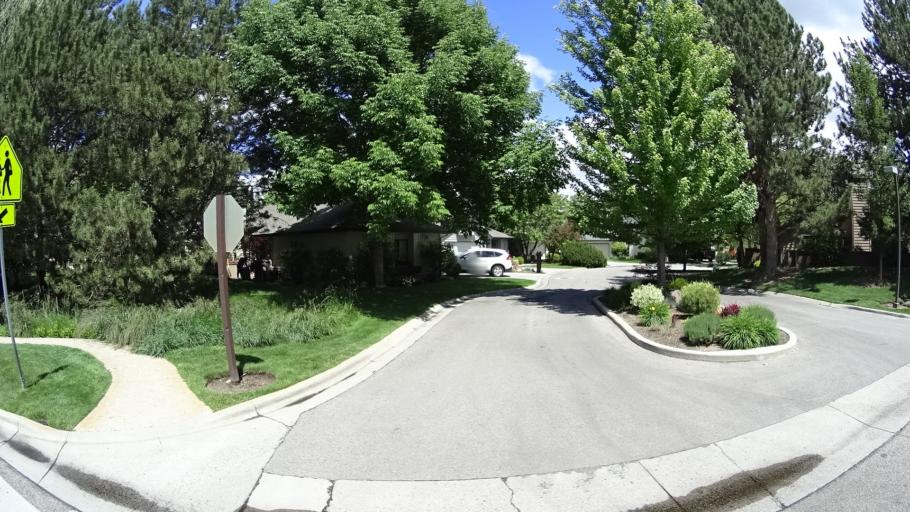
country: US
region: Idaho
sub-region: Ada County
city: Boise
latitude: 43.5875
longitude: -116.1664
